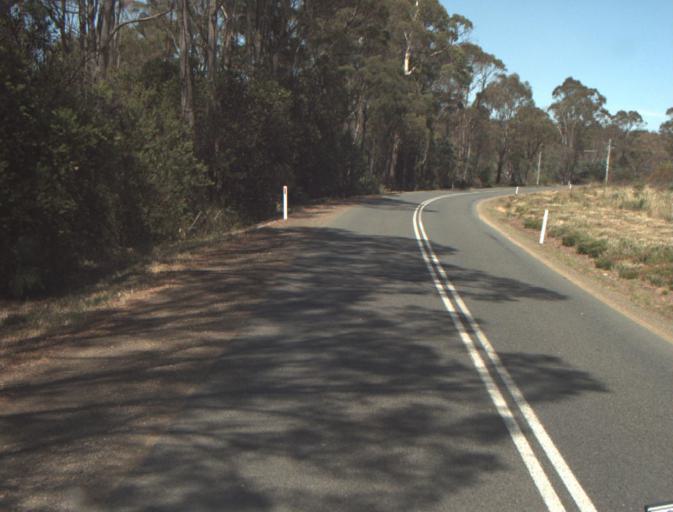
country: AU
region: Tasmania
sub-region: Launceston
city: Mayfield
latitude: -41.3278
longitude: 147.1395
